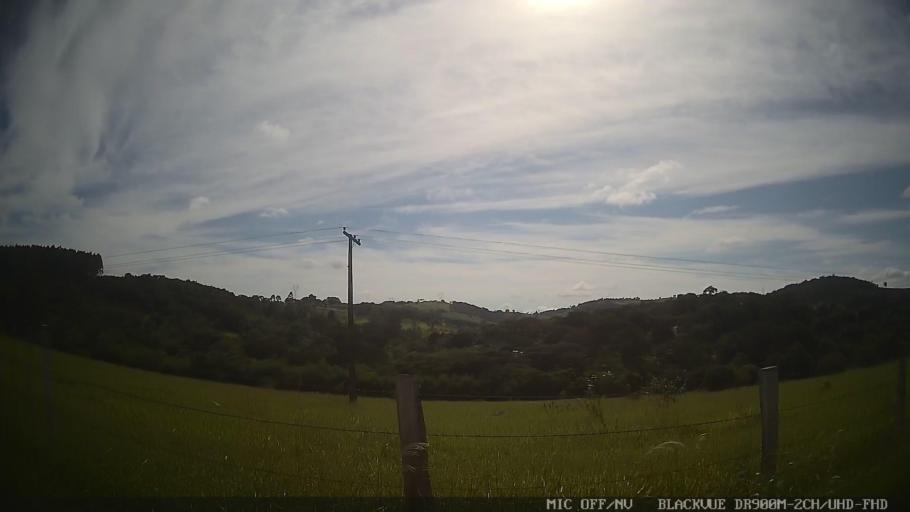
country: BR
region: Sao Paulo
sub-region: Jarinu
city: Jarinu
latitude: -23.0535
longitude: -46.6423
